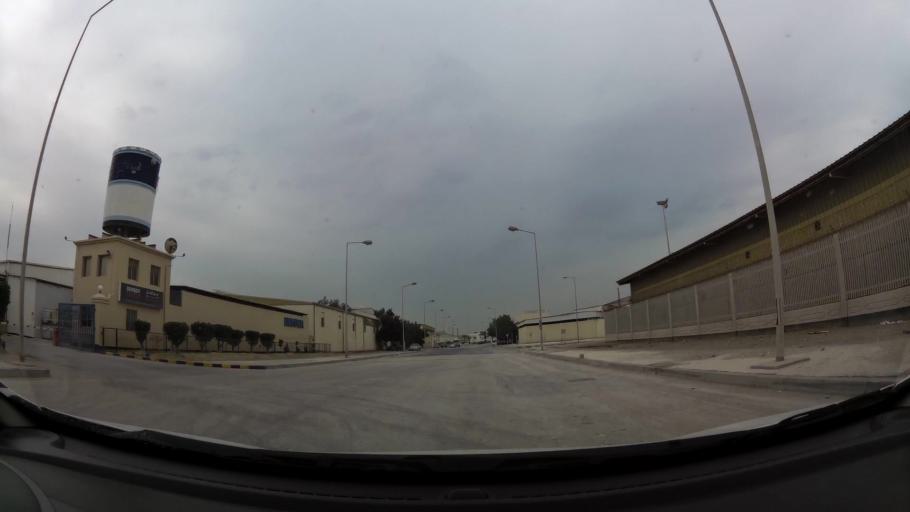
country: BH
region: Northern
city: Sitrah
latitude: 26.1825
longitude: 50.6197
